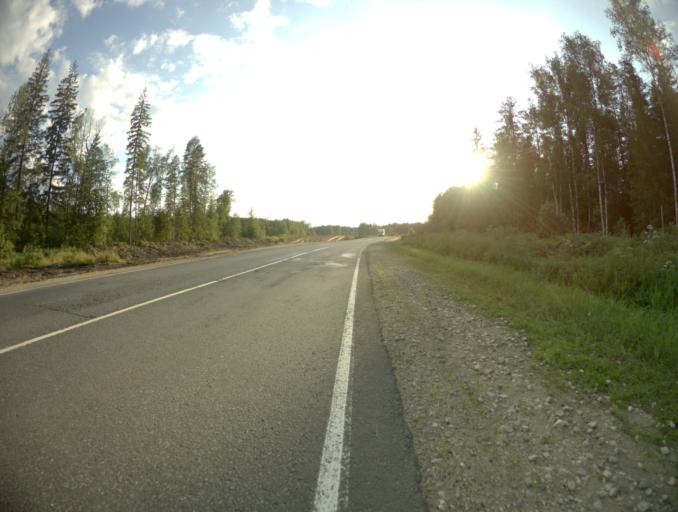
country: RU
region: Vladimir
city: Orgtrud
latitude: 56.0109
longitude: 40.6089
